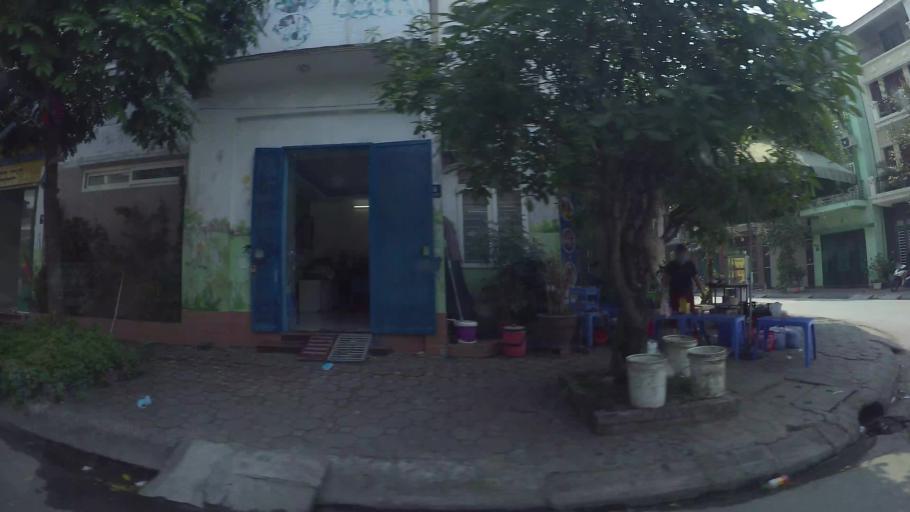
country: VN
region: Ha Noi
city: Ha Dong
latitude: 20.9727
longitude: 105.7986
